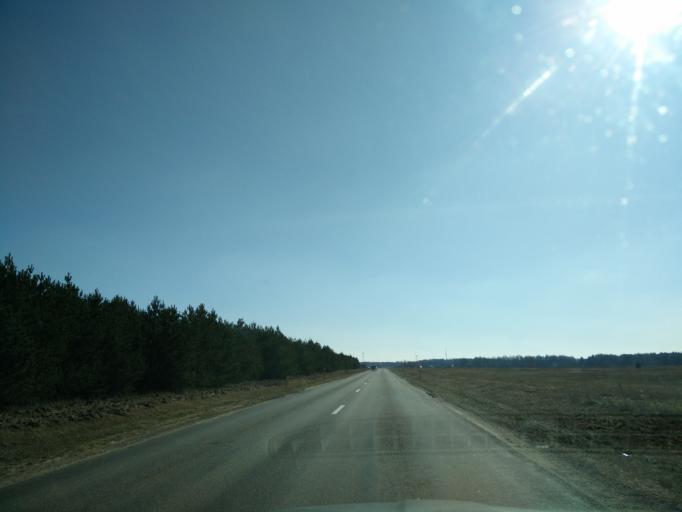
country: LT
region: Klaipedos apskritis
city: Silute
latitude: 55.3244
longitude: 21.5259
